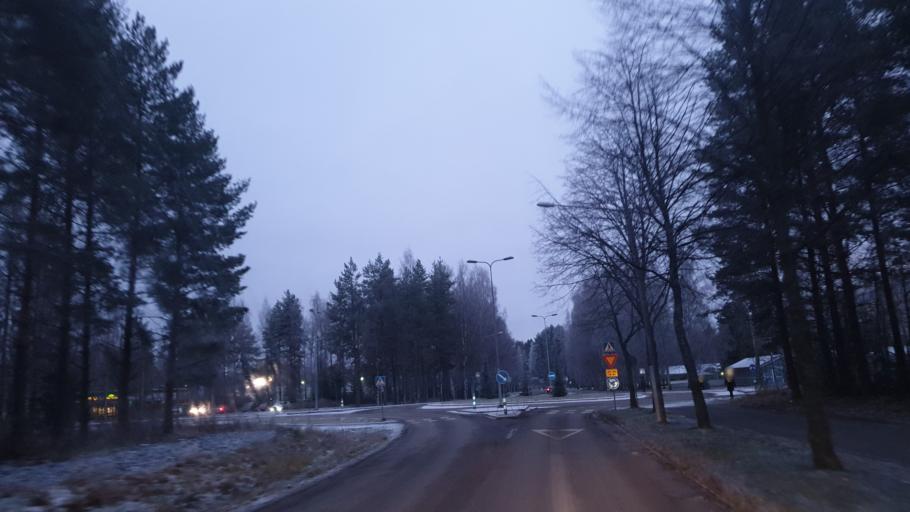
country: FI
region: Southern Ostrobothnia
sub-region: Seinaejoki
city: Seinaejoki
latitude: 62.7722
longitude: 22.8766
